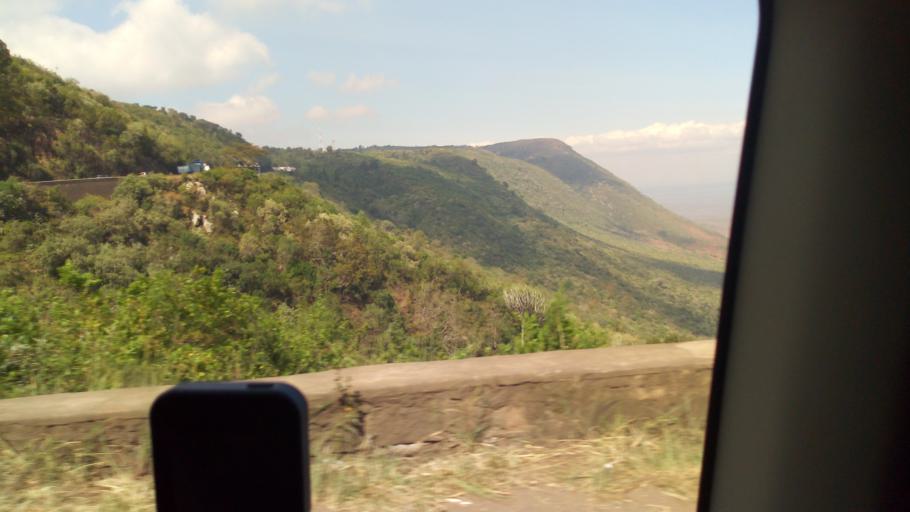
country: KE
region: Kiambu
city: Limuru
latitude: -1.0602
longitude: 36.6040
